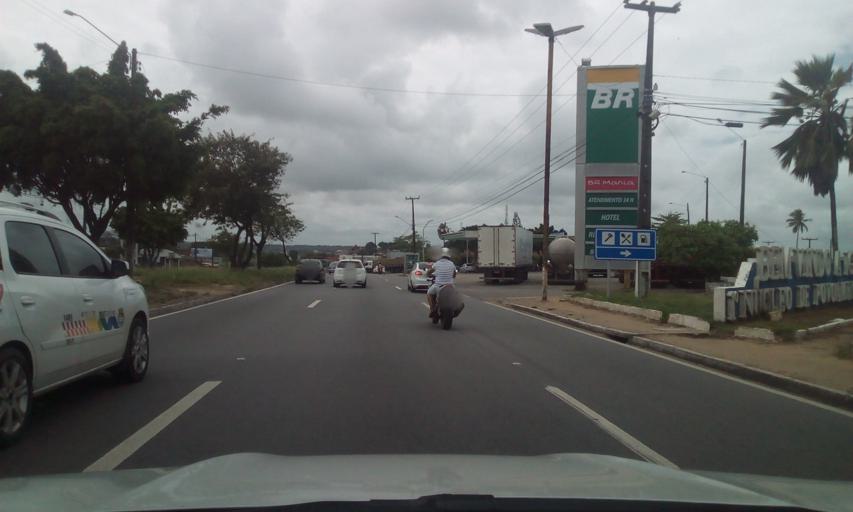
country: BR
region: Pernambuco
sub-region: Igarassu
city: Igarassu
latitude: -7.8496
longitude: -34.9094
